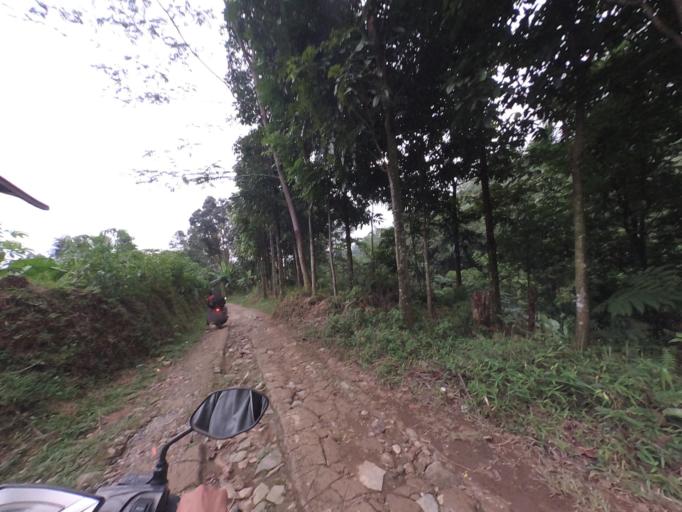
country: ID
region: West Java
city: Cicurug
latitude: -6.7015
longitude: 106.6611
